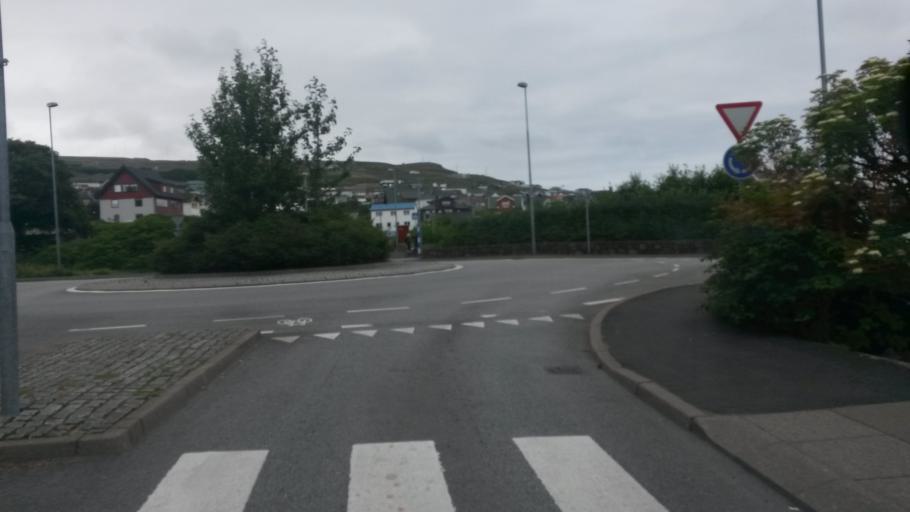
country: FO
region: Streymoy
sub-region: Torshavn
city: Torshavn
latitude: 62.0067
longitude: -6.7849
